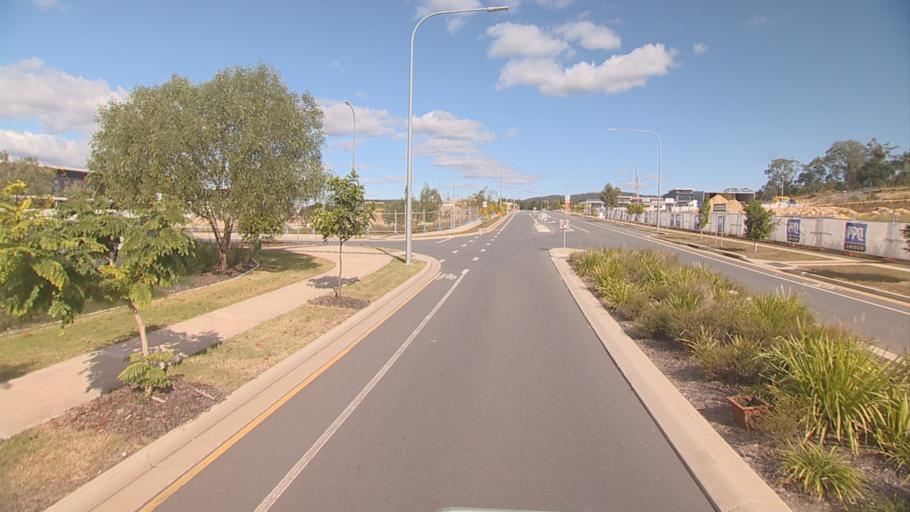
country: AU
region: Queensland
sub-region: Logan
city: Chambers Flat
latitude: -27.8026
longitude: 153.1012
